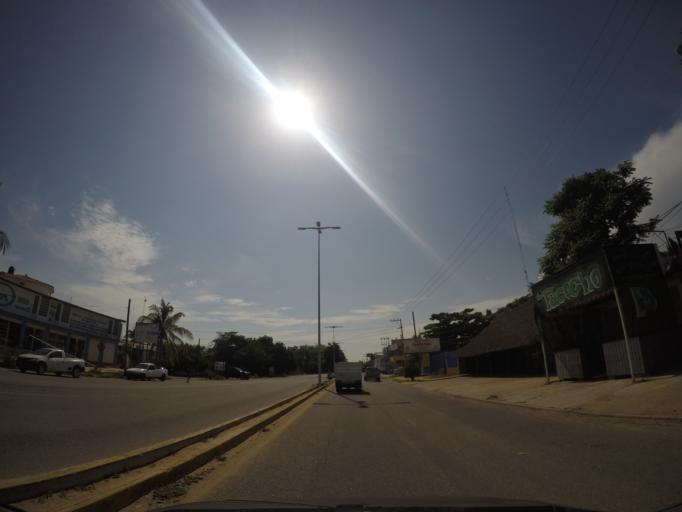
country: MX
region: Oaxaca
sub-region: San Pedro Mixtepec -Dto. 22 -
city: Puerto Escondido
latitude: 15.8678
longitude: -97.0803
